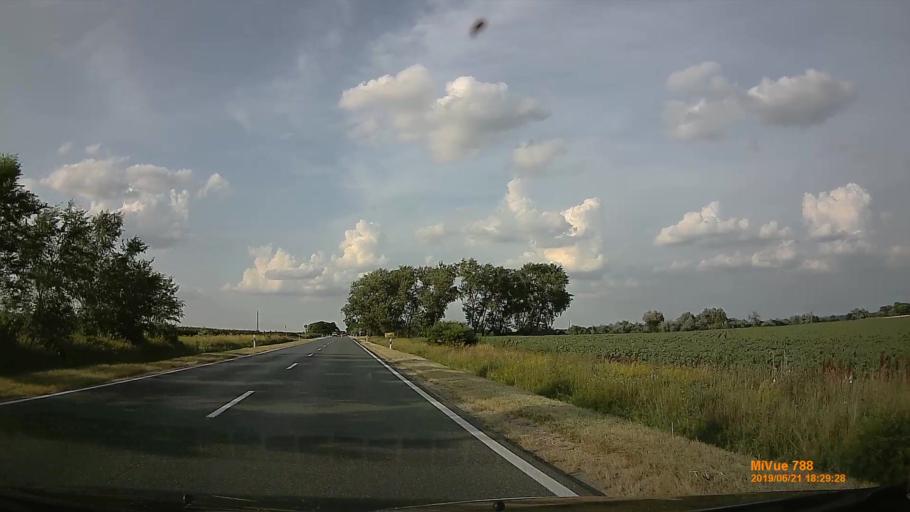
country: HU
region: Tolna
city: Dunafoldvar
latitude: 46.7406
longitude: 18.8847
